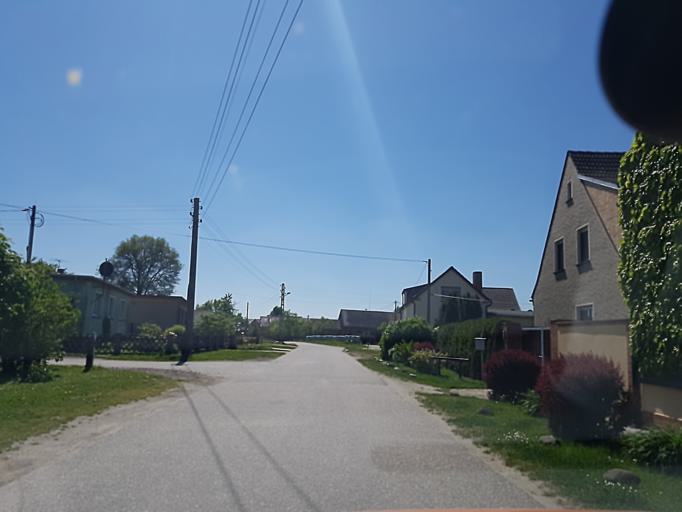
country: DE
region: Brandenburg
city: Sallgast
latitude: 51.6196
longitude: 13.8088
